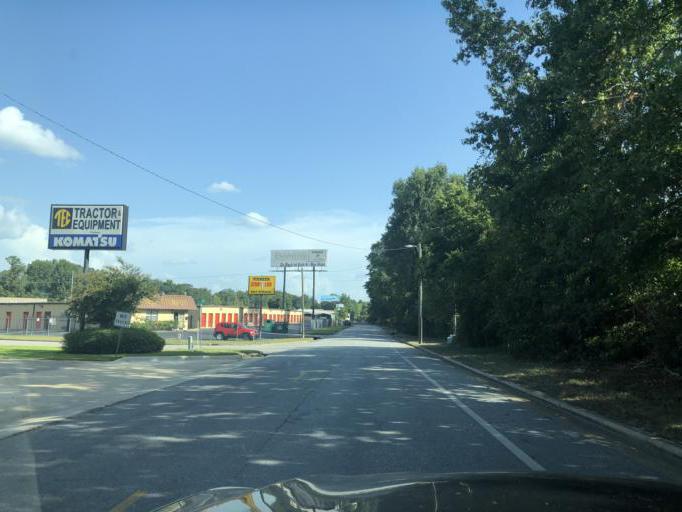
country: US
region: Georgia
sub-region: Muscogee County
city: Columbus
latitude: 32.4765
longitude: -84.9357
